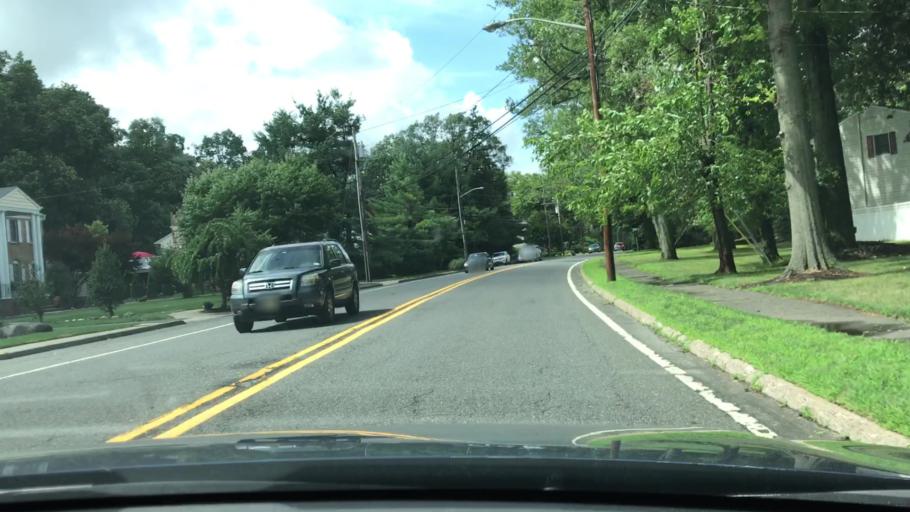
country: US
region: New Jersey
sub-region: Bergen County
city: Wyckoff
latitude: 41.0151
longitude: -74.1666
